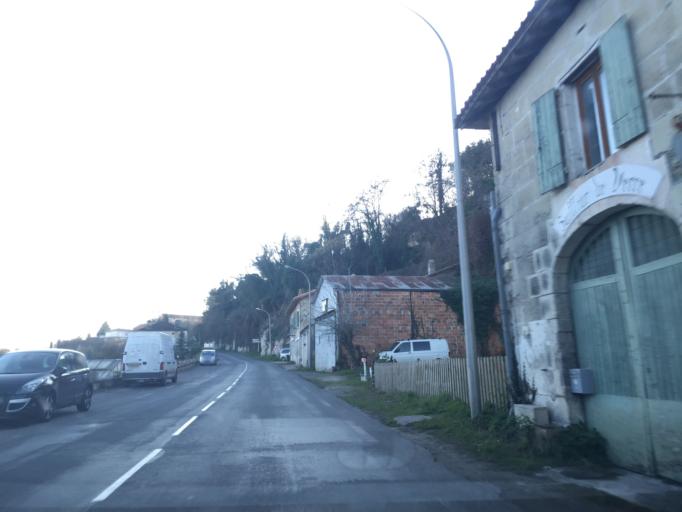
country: FR
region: Aquitaine
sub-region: Departement de la Dordogne
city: Saint-Aulaye
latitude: 45.2704
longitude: 0.1714
